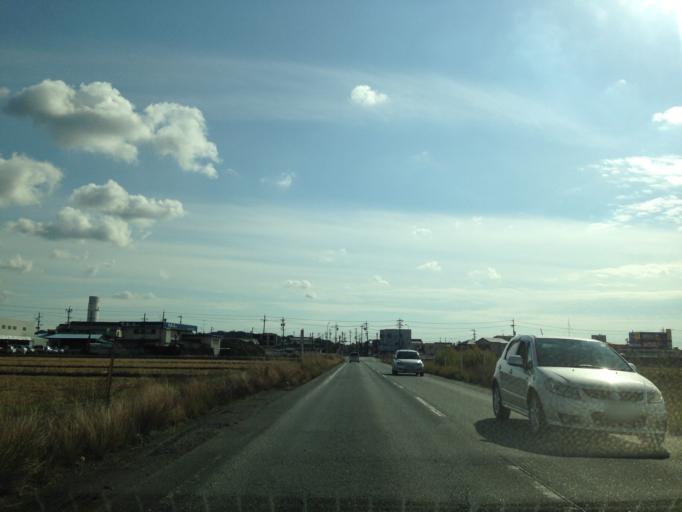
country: JP
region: Shizuoka
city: Fukuroi
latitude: 34.7546
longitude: 137.9274
